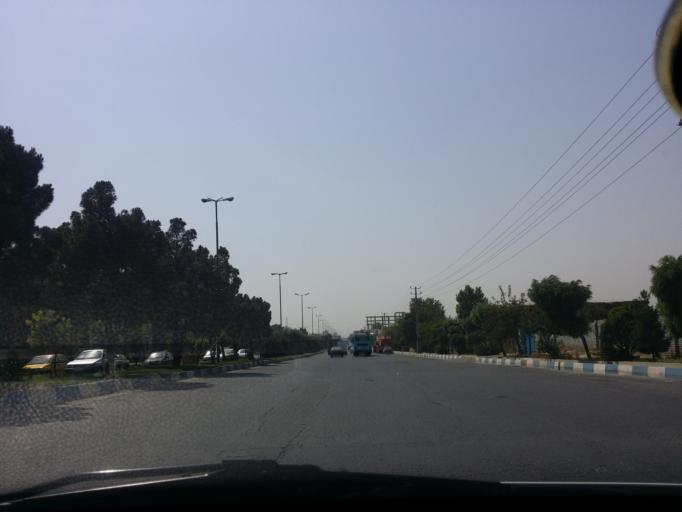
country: IR
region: Alborz
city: Karaj
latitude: 35.8546
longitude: 50.8982
